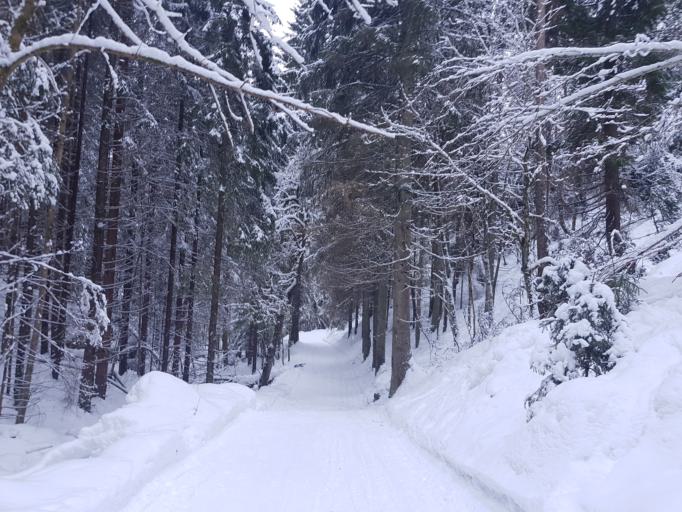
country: NO
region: Akershus
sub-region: Lorenskog
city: Kjenn
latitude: 59.8982
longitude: 10.8754
